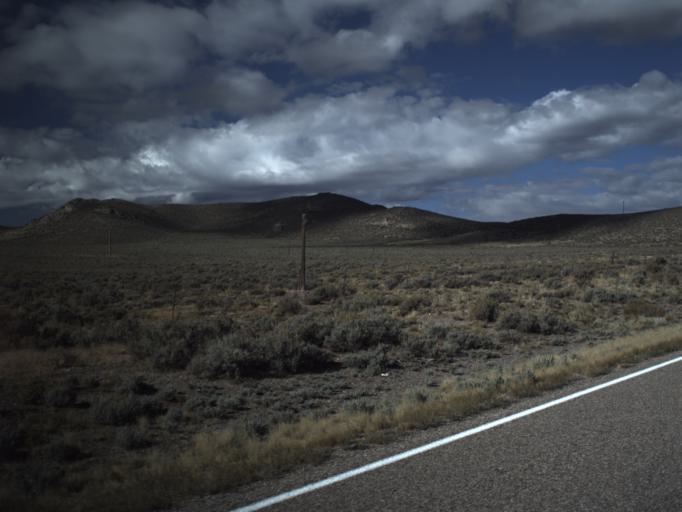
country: US
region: Utah
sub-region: Beaver County
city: Milford
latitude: 38.4216
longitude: -113.1022
